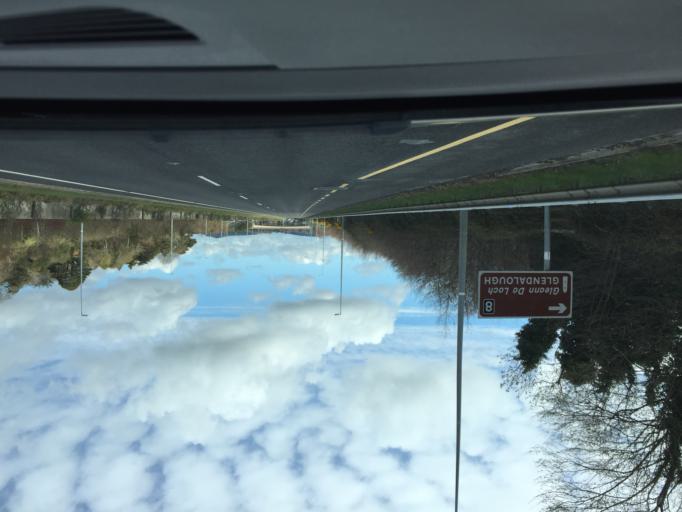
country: IE
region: Leinster
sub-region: Wicklow
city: Kilmacanoge
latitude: 53.1628
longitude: -6.1316
